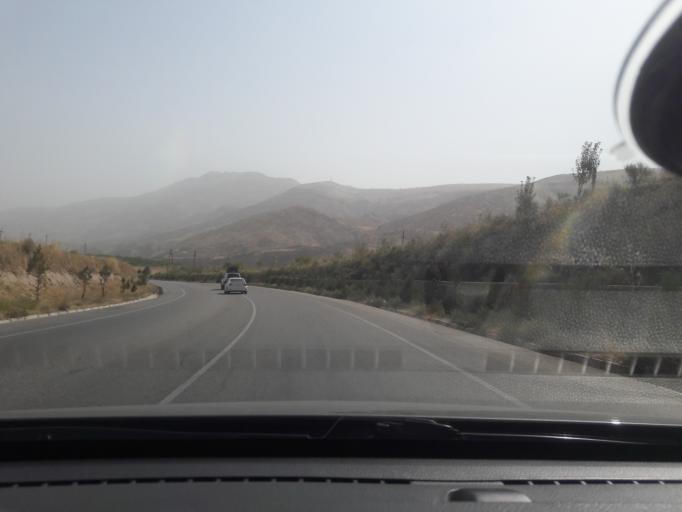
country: TJ
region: Republican Subordination
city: Vahdat
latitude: 38.4879
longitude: 69.1642
